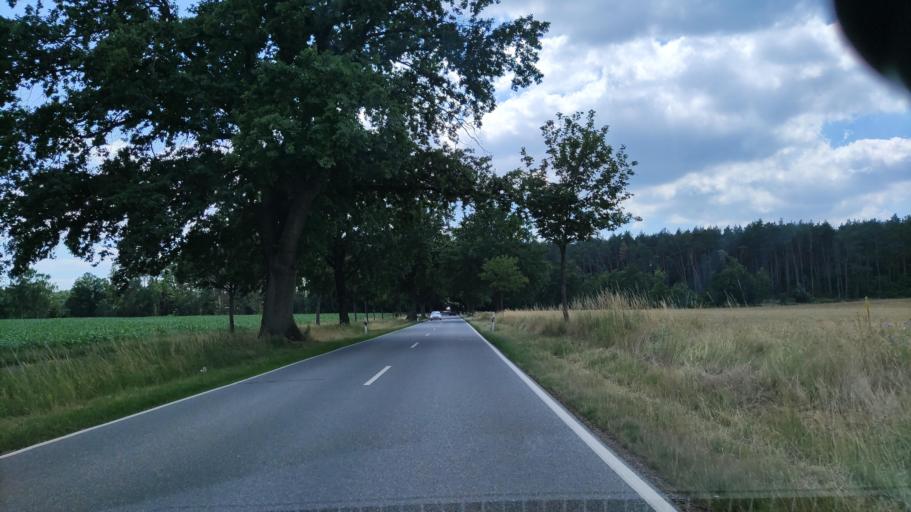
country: DE
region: Mecklenburg-Vorpommern
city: Hagenow
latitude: 53.3876
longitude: 11.1603
